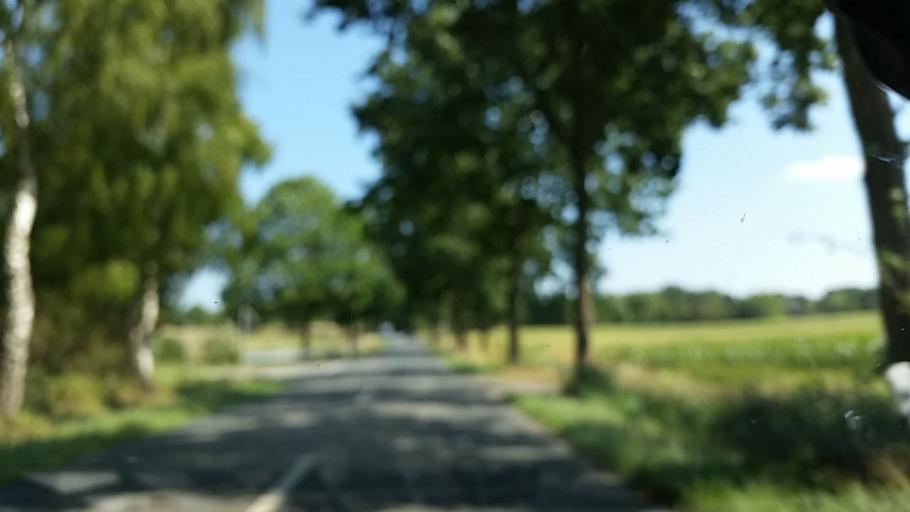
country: DE
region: Lower Saxony
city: Vastorf
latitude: 53.1936
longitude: 10.5420
